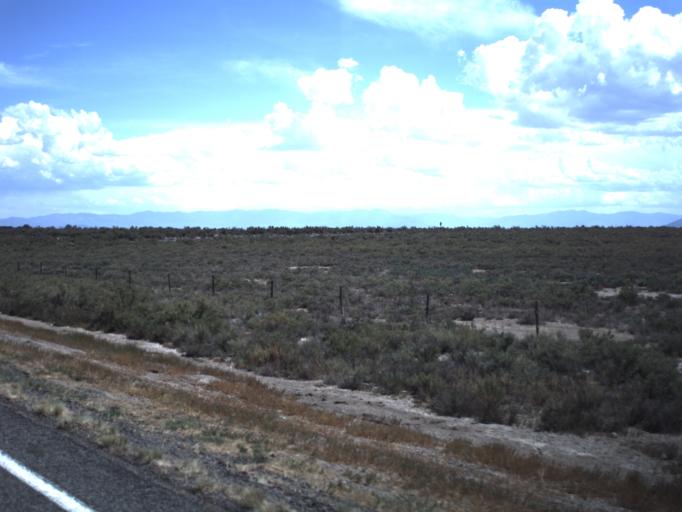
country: US
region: Utah
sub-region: Millard County
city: Delta
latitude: 39.3309
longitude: -112.7105
